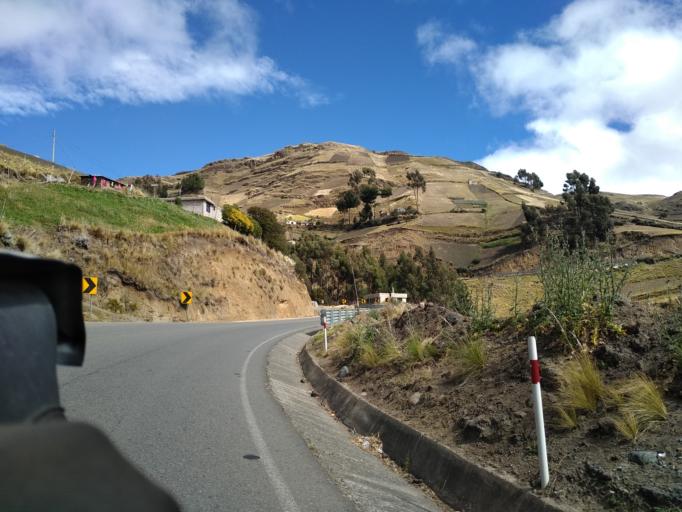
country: EC
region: Cotopaxi
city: Pujili
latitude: -0.9618
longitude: -78.9100
